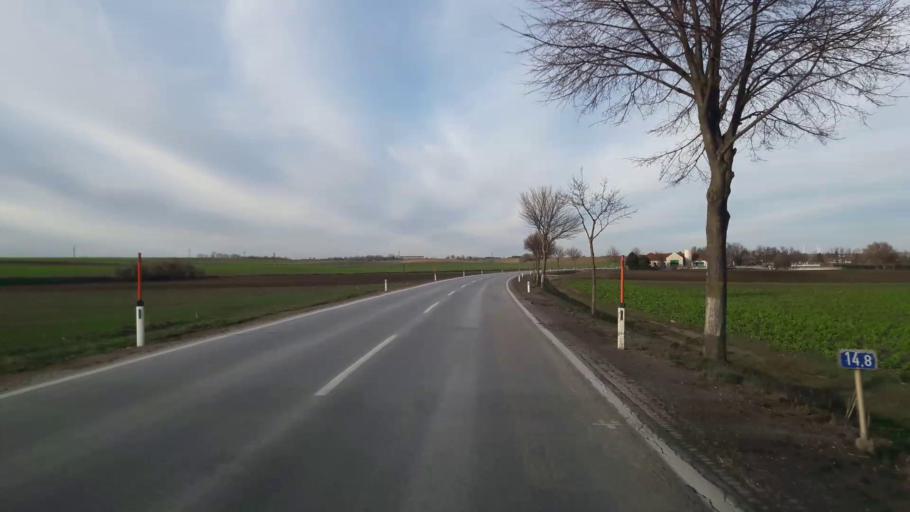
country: AT
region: Lower Austria
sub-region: Politischer Bezirk Ganserndorf
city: Bad Pirawarth
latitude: 48.4351
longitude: 16.6079
